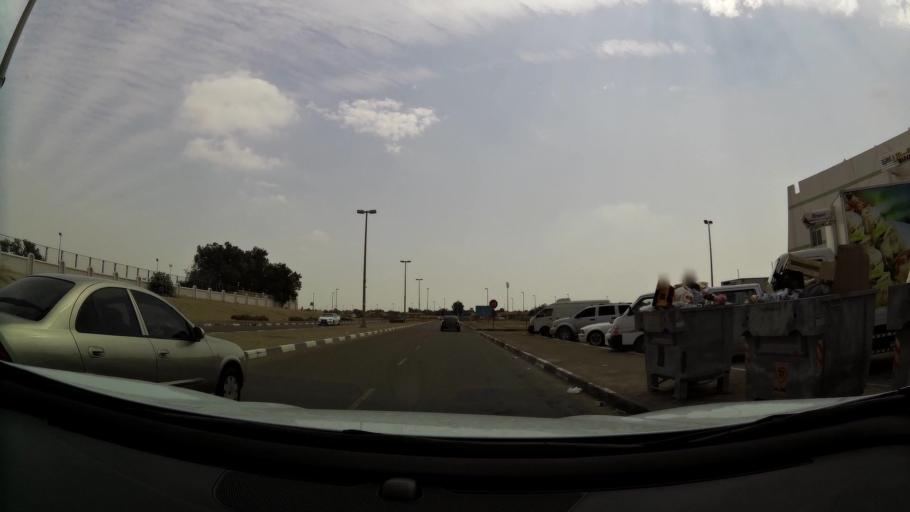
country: AE
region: Abu Dhabi
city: Abu Dhabi
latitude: 24.5251
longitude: 54.6771
